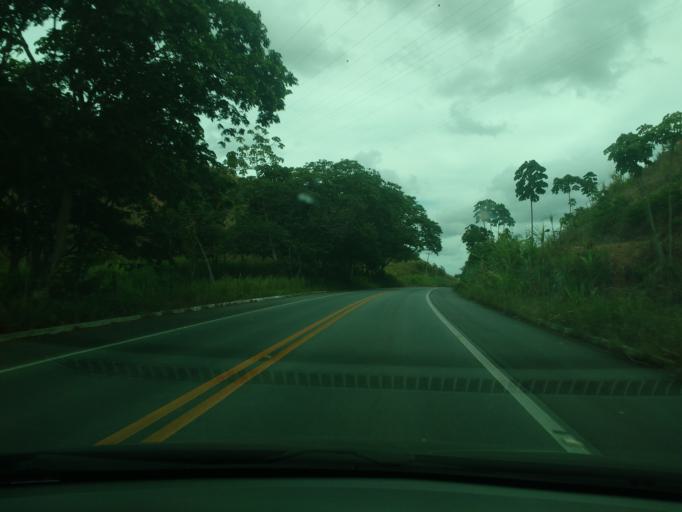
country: BR
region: Alagoas
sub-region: Murici
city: Murici
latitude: -9.2701
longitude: -35.9639
